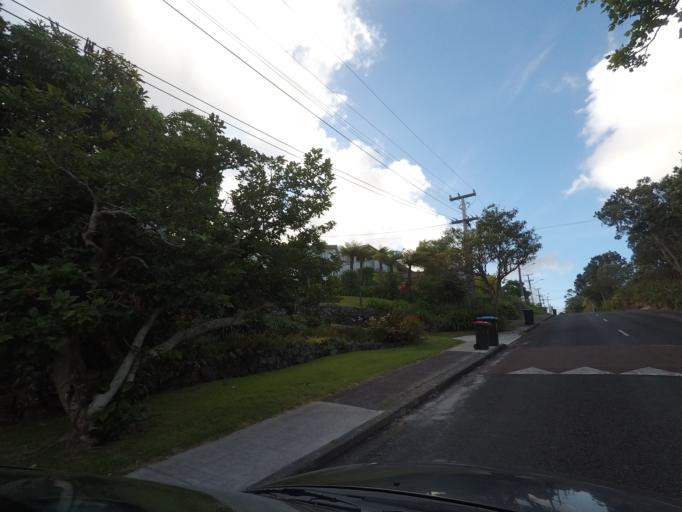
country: NZ
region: Auckland
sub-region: Auckland
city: Auckland
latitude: -36.9242
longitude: 174.7579
